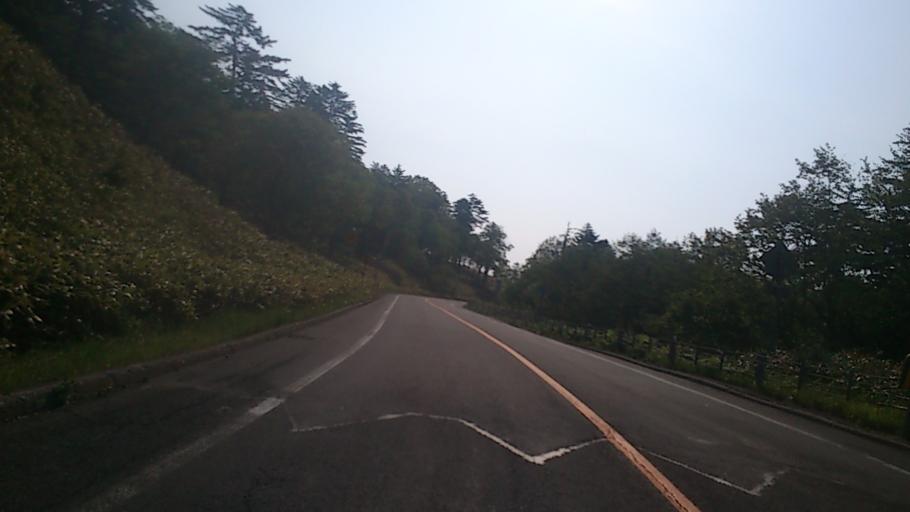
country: JP
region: Hokkaido
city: Bihoro
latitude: 43.4432
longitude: 144.1908
